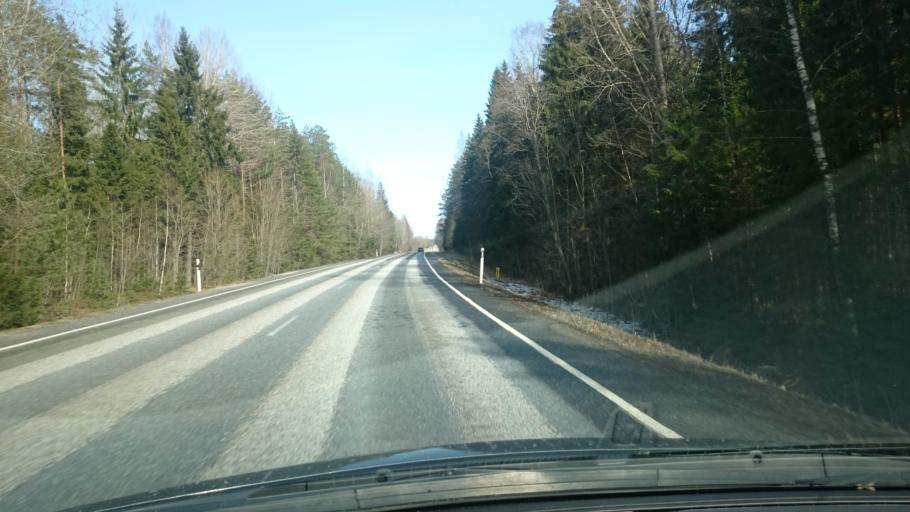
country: EE
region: Jaervamaa
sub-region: Tueri vald
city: Sarevere
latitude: 58.7420
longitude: 25.3043
